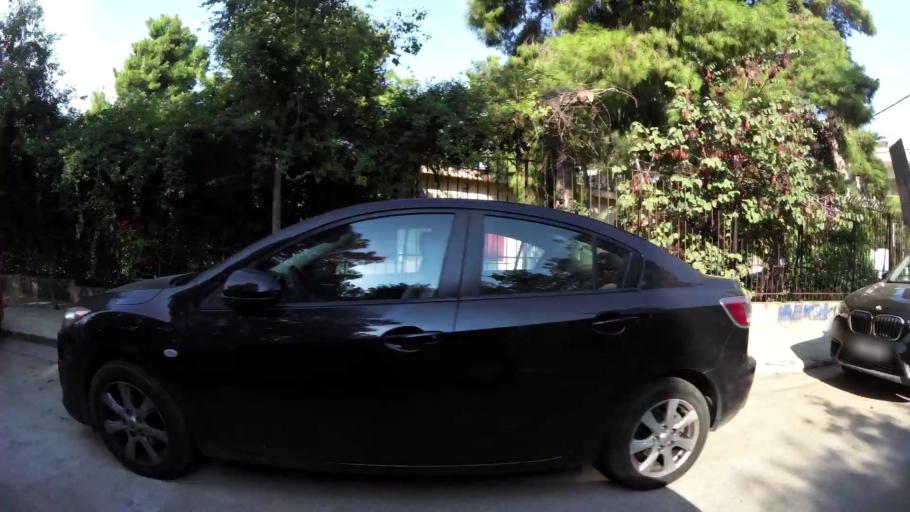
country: GR
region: Attica
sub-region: Nomarchia Athinas
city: Nea Smyrni
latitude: 37.9398
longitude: 23.7099
